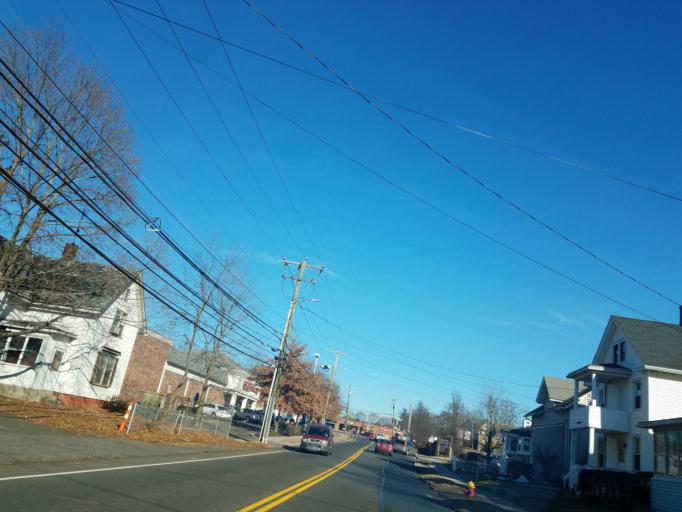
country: US
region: Connecticut
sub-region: New Haven County
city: Meriden
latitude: 41.5397
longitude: -72.8226
